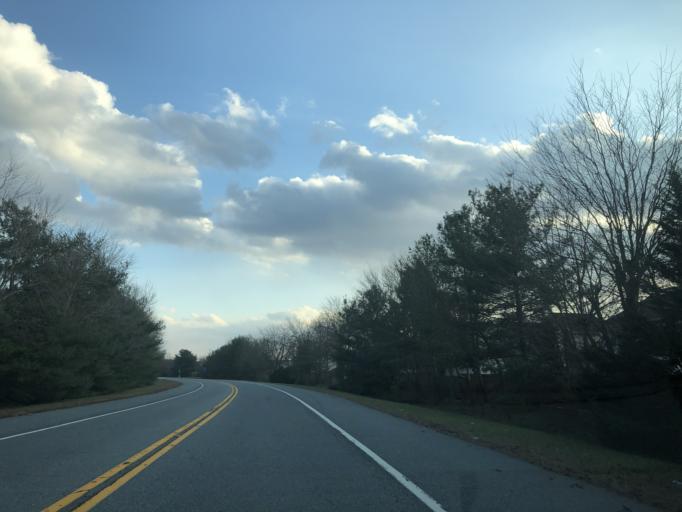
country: US
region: Delaware
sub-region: New Castle County
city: Bear
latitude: 39.6310
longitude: -75.6496
